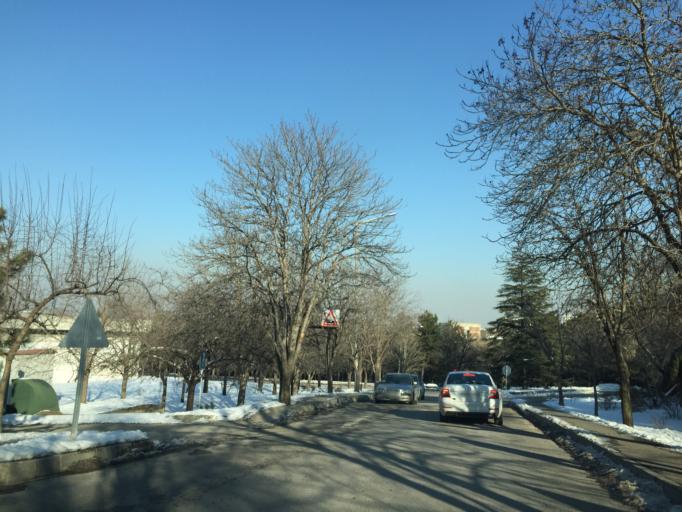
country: TR
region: Ankara
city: Ankara
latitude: 39.8874
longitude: 32.7834
